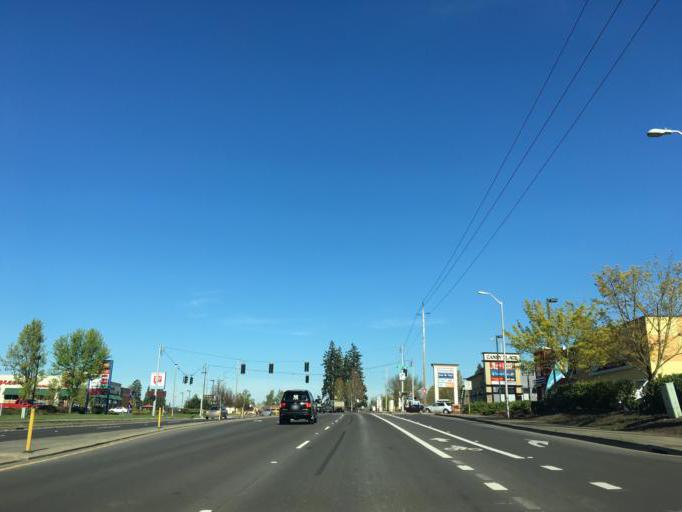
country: US
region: Oregon
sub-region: Clackamas County
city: Canby
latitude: 45.2560
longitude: -122.7053
